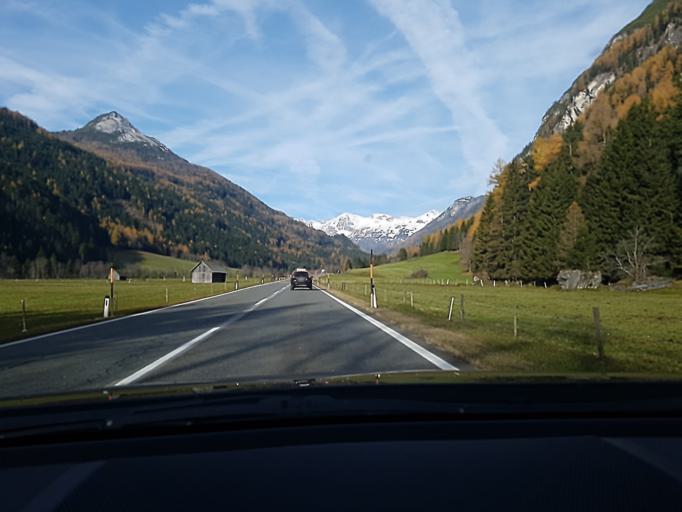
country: AT
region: Salzburg
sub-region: Politischer Bezirk Tamsweg
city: Tweng
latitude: 47.1859
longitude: 13.6104
